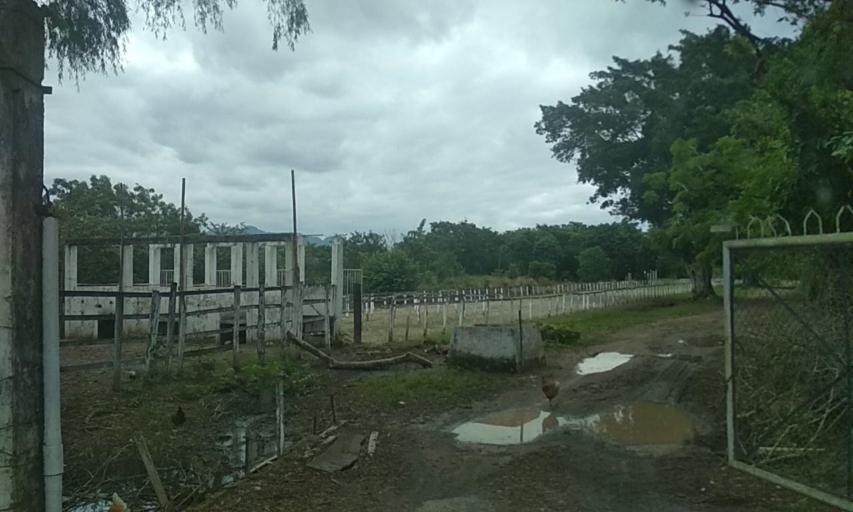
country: MX
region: Veracruz
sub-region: Martinez de la Torre
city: El Progreso
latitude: 20.0989
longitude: -97.0066
